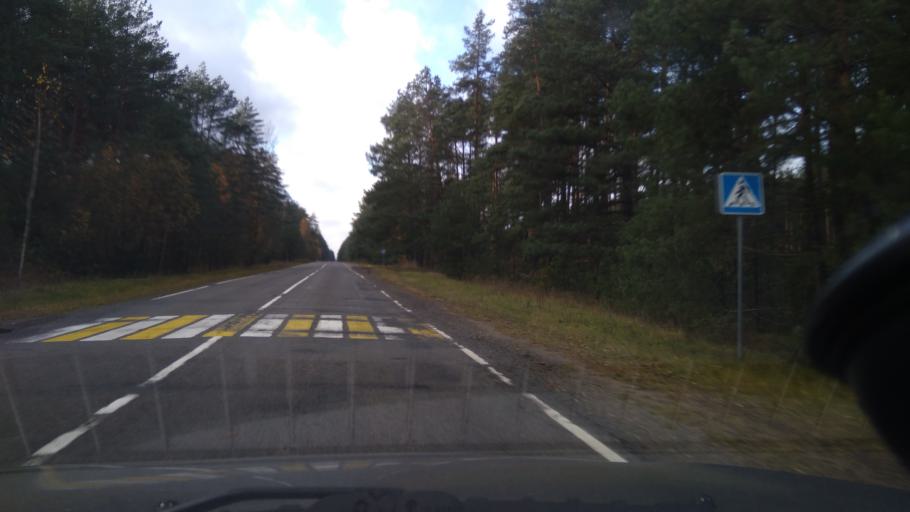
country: BY
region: Minsk
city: Slutsk
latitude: 53.2294
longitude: 27.7062
